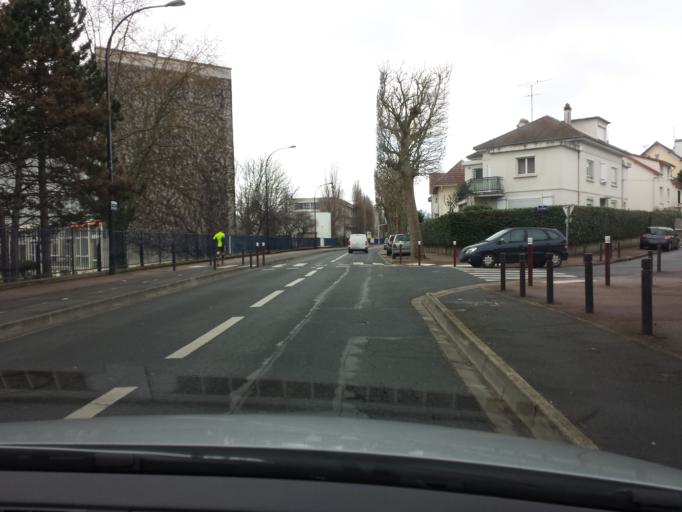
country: FR
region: Ile-de-France
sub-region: Departement du Val-de-Marne
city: L'Hay-les-Roses
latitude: 48.7905
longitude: 2.3270
